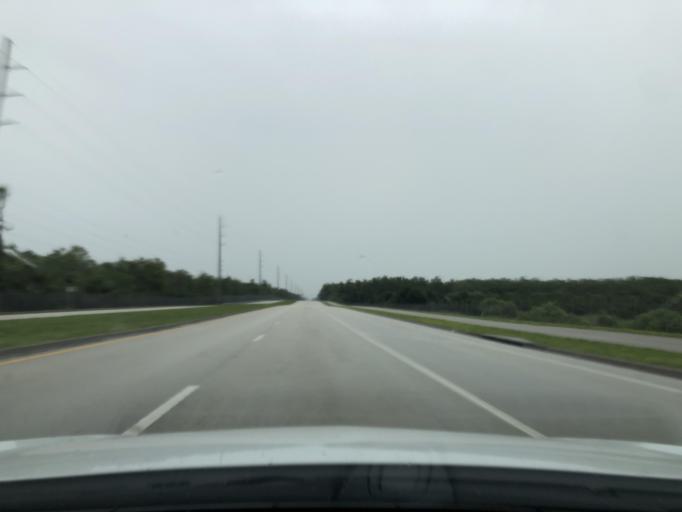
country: US
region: Florida
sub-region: Collier County
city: Orangetree
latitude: 26.2940
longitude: -81.4651
